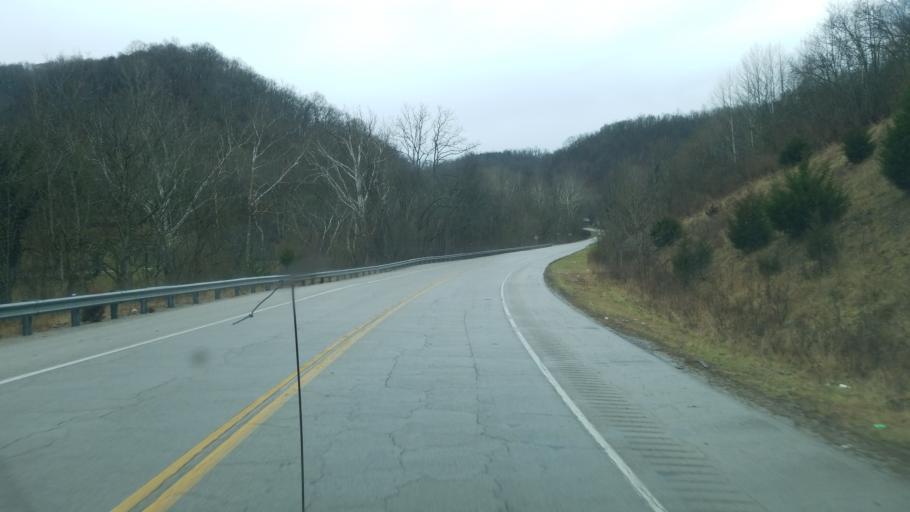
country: US
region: Kentucky
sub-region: Mason County
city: Maysville
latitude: 38.6321
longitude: -83.7069
